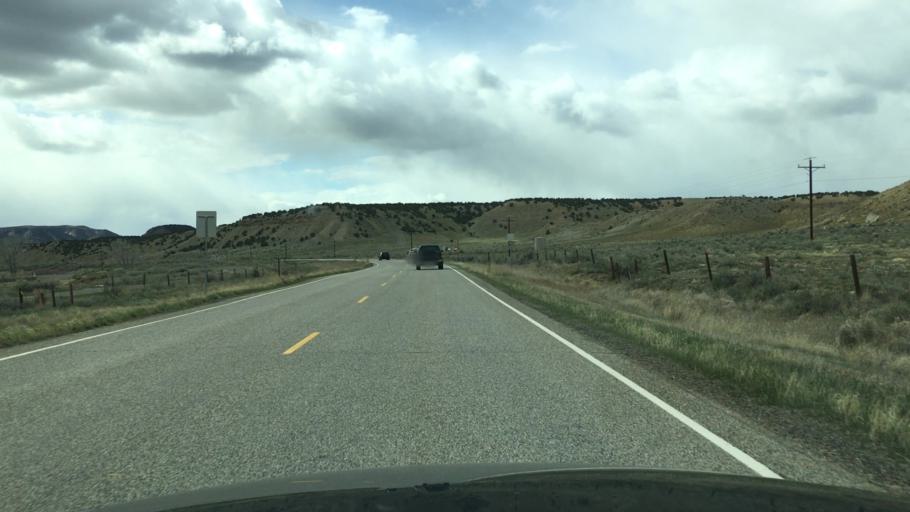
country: US
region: Colorado
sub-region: Rio Blanco County
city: Meeker
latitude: 40.0911
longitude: -108.2066
